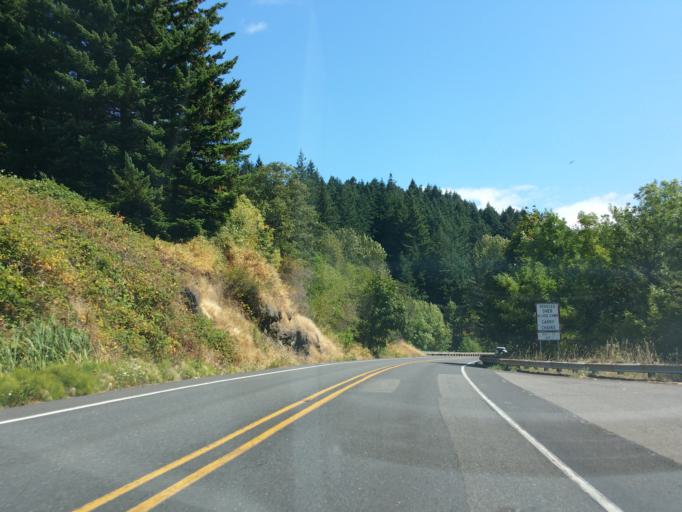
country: US
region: Washington
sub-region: Skamania County
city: Stevenson
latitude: 45.6990
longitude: -121.8734
